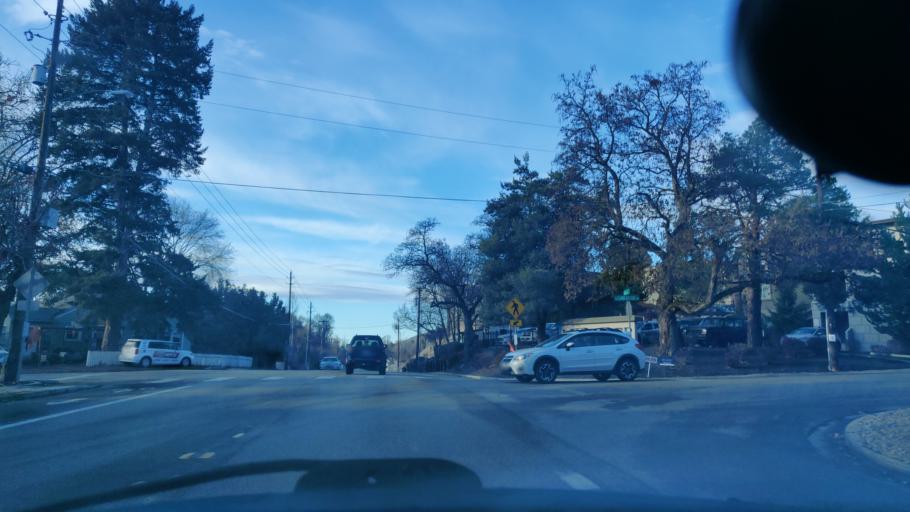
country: US
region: Idaho
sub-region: Ada County
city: Boise
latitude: 43.6432
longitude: -116.2141
